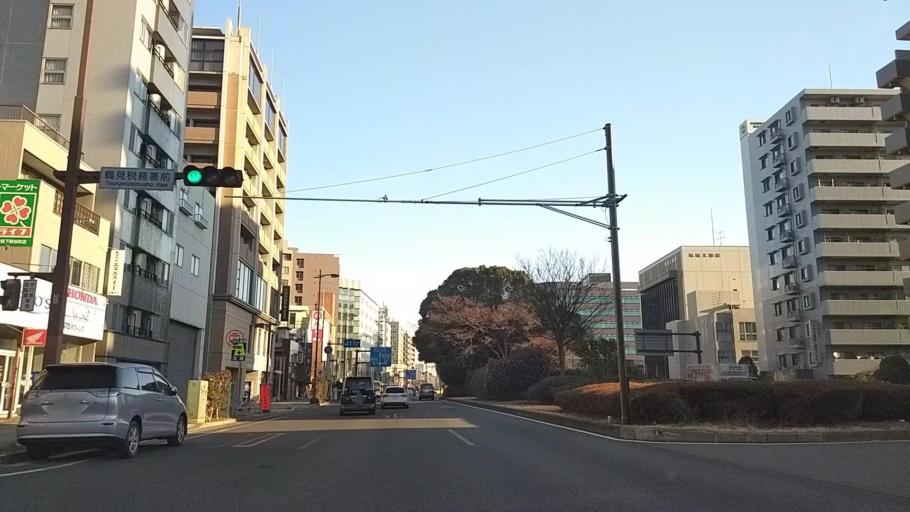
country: JP
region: Kanagawa
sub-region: Kawasaki-shi
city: Kawasaki
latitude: 35.5062
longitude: 139.6796
